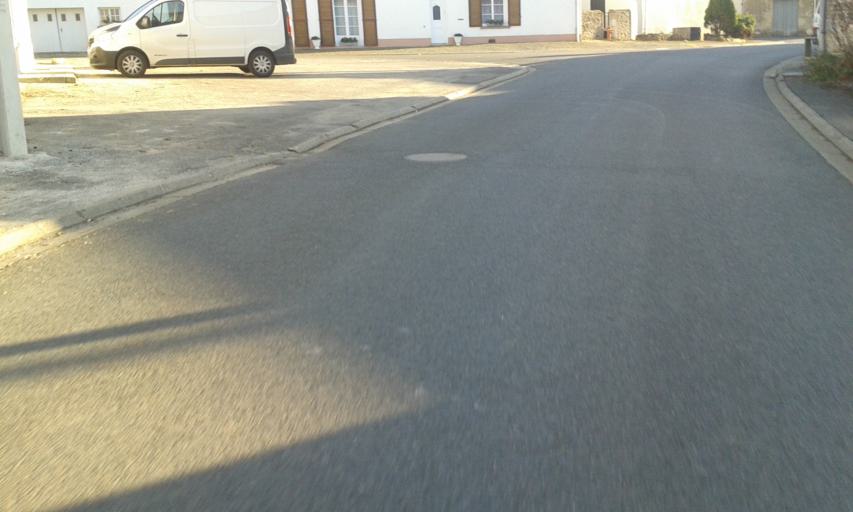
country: FR
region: Centre
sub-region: Departement du Loir-et-Cher
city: Ouzouer-le-Marche
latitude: 47.8793
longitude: 1.4198
